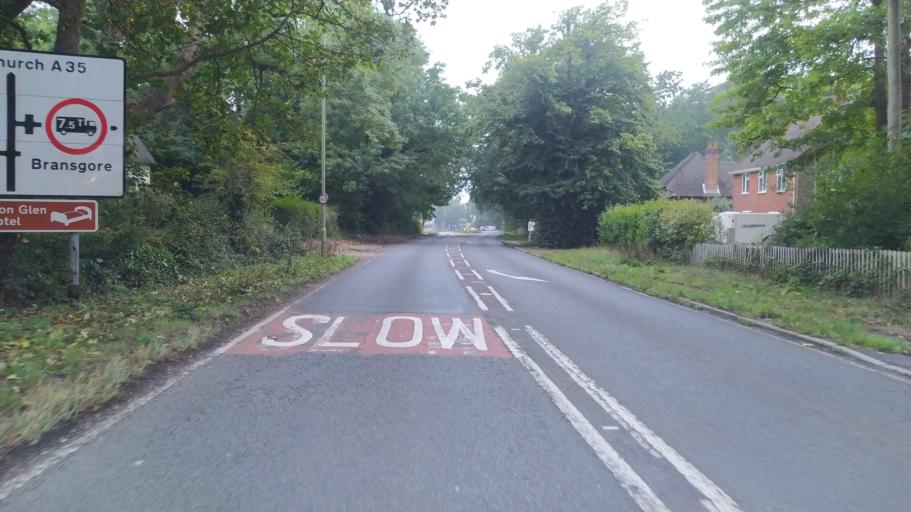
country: GB
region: England
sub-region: Hampshire
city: Bransgore
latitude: 50.7574
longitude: -1.7067
